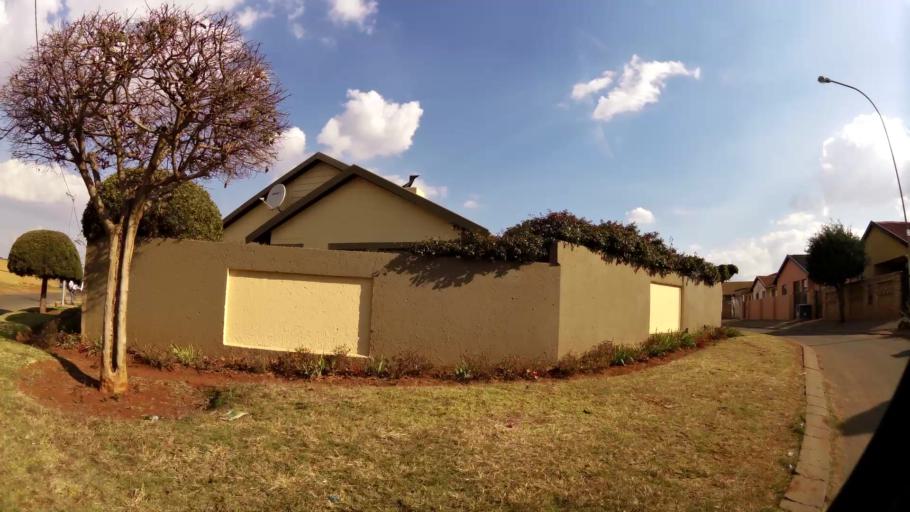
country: ZA
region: Gauteng
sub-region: City of Johannesburg Metropolitan Municipality
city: Roodepoort
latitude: -26.2108
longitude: 27.8680
